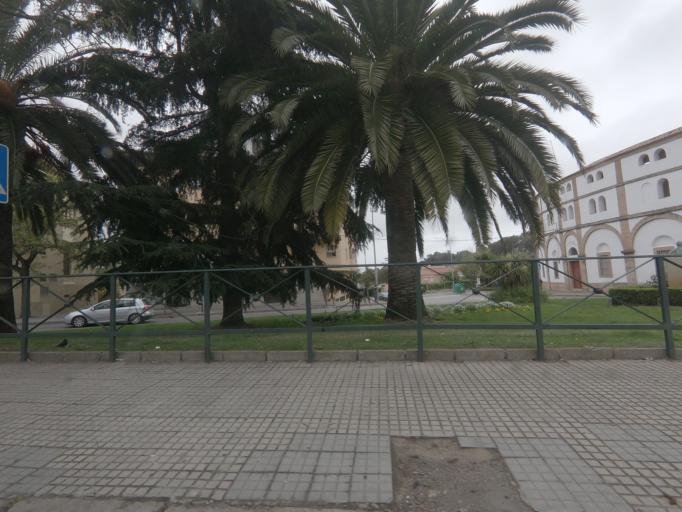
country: ES
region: Extremadura
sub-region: Provincia de Caceres
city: Caceres
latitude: 39.4797
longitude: -6.3758
